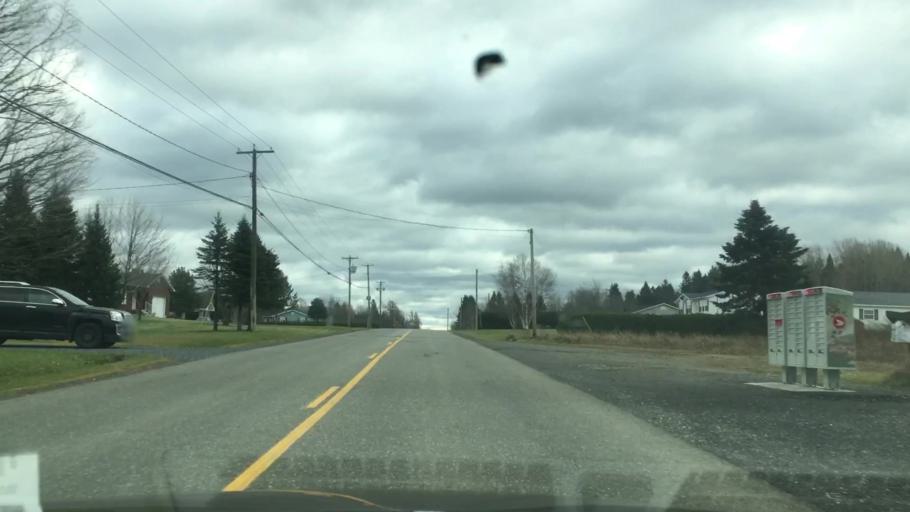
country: US
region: Maine
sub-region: Aroostook County
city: Fort Fairfield
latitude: 46.7570
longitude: -67.7664
